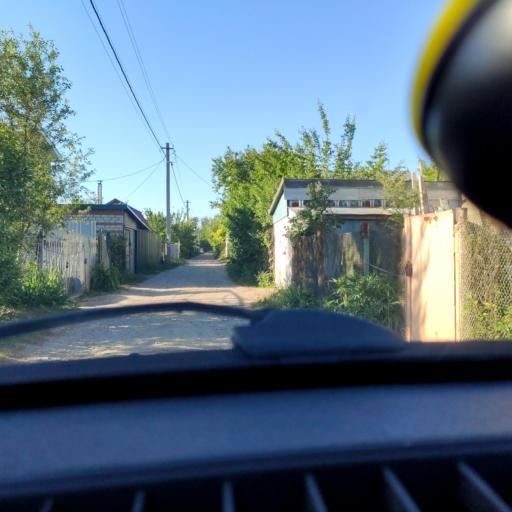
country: RU
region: Samara
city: Tol'yatti
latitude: 53.5956
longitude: 49.3149
